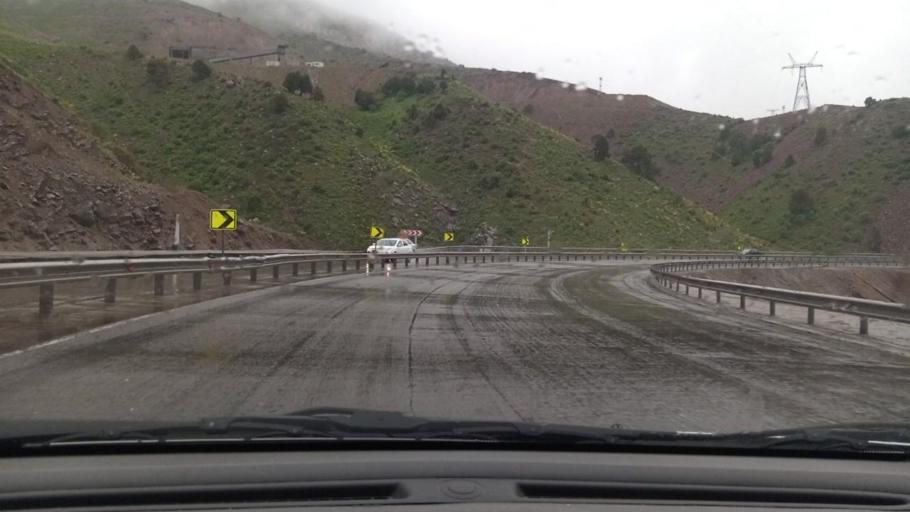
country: UZ
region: Toshkent
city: Angren
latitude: 41.0904
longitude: 70.5346
